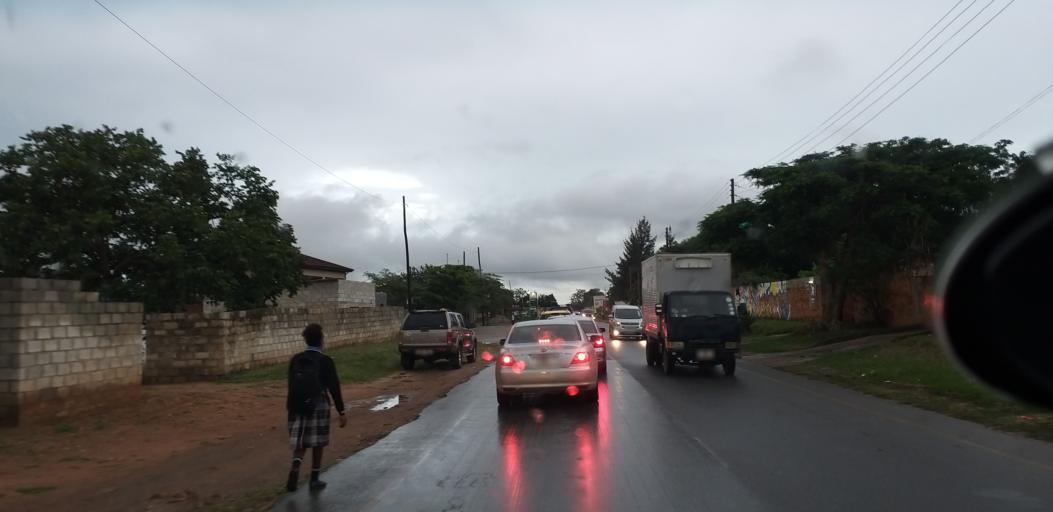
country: ZM
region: Lusaka
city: Lusaka
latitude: -15.4154
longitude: 28.3681
